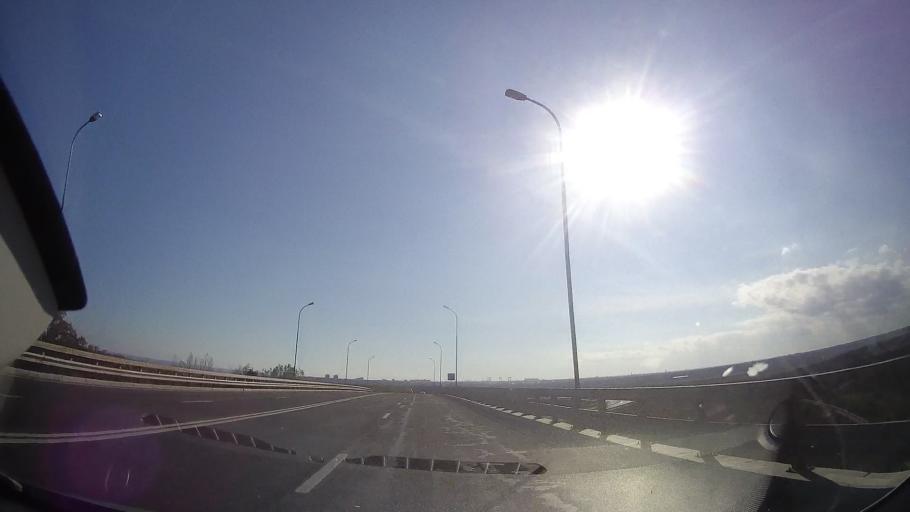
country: RO
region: Constanta
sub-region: Comuna Douazeci si Trei August
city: Dulcesti
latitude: 43.8580
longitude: 28.5758
